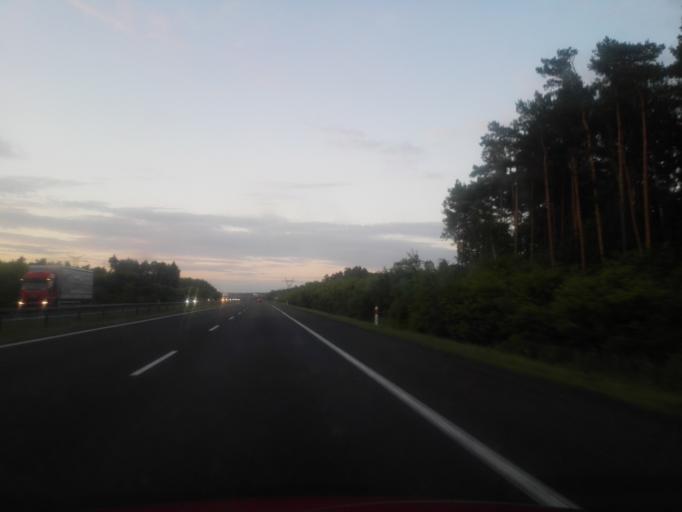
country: PL
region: Lodz Voivodeship
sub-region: Powiat radomszczanski
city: Radomsko
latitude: 51.0410
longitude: 19.3444
